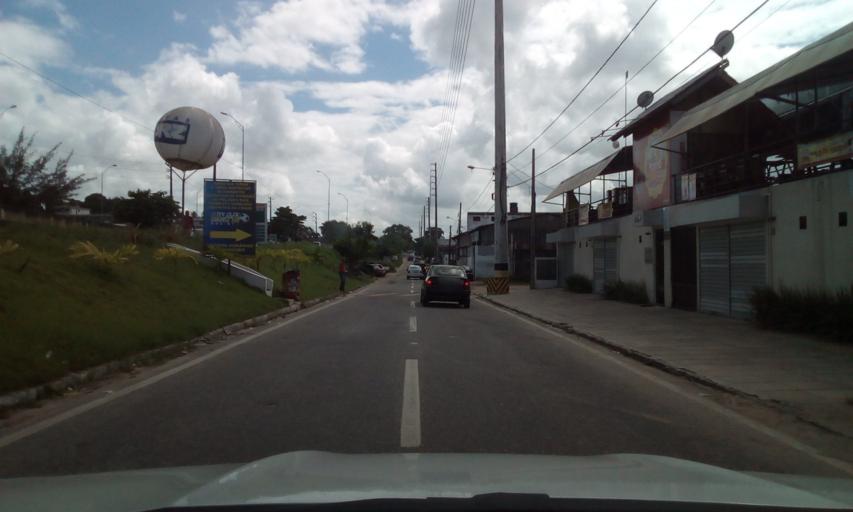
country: BR
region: Paraiba
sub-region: Bayeux
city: Bayeux
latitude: -7.1306
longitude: -34.9335
